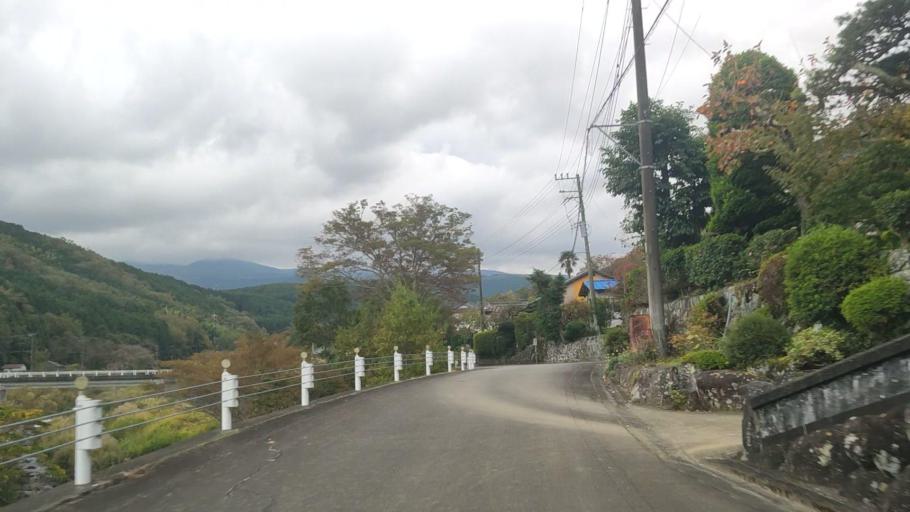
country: JP
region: Shizuoka
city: Ito
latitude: 34.9307
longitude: 138.9901
